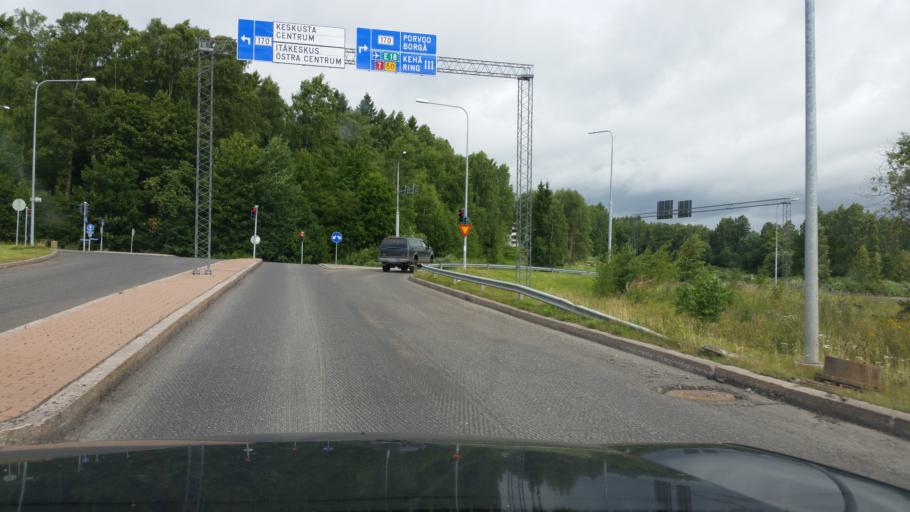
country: FI
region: Uusimaa
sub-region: Helsinki
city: Vantaa
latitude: 60.2323
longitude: 25.1335
